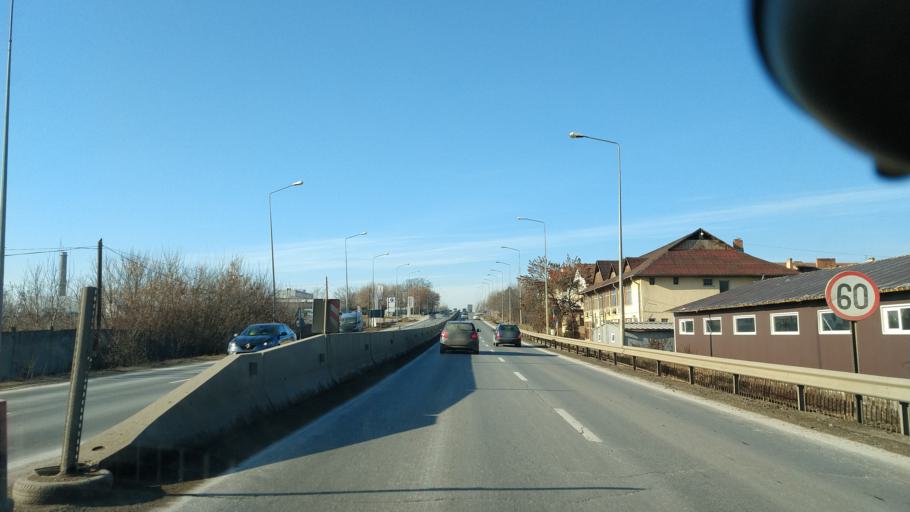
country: RO
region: Iasi
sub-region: Comuna Valea Lupului
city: Valea Lupului
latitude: 47.1755
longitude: 27.4976
